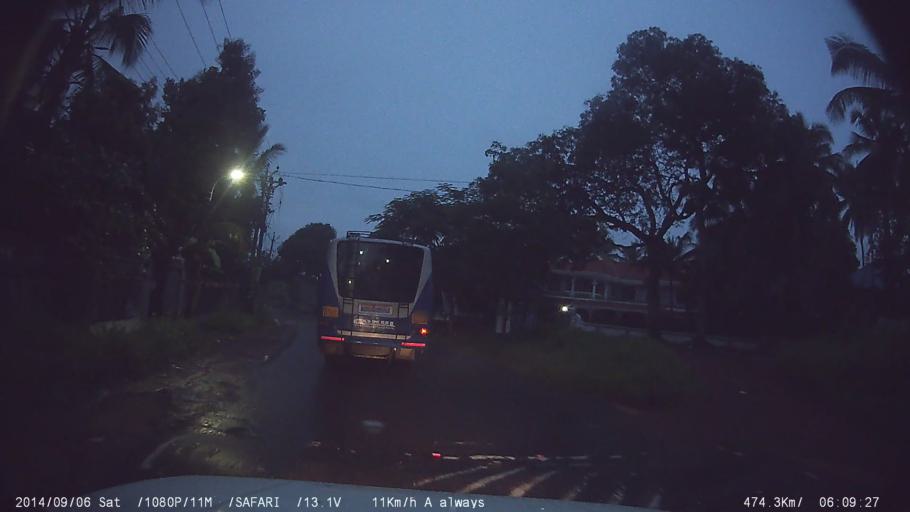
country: IN
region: Kerala
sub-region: Alappuzha
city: Arukutti
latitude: 9.9191
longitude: 76.3889
